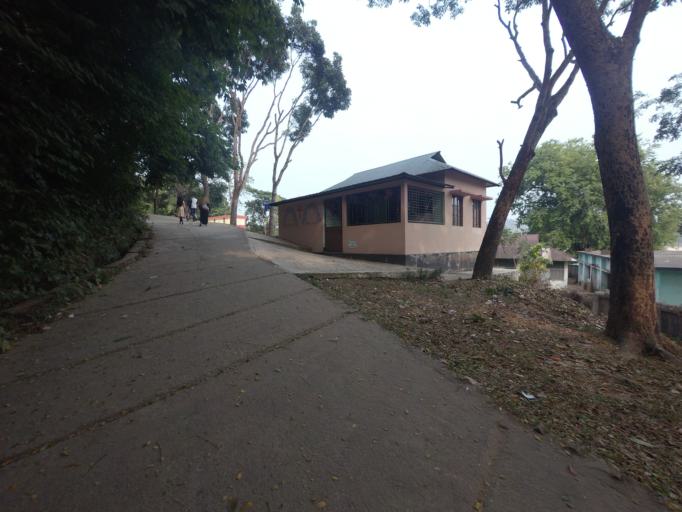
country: BD
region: Dhaka
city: Netrakona
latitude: 25.1715
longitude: 90.6589
